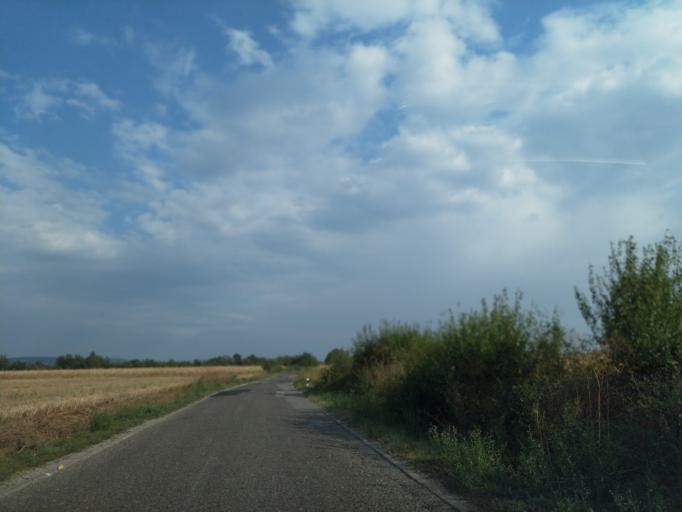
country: RS
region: Central Serbia
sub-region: Pomoravski Okrug
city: Paracin
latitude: 43.8472
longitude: 21.4653
